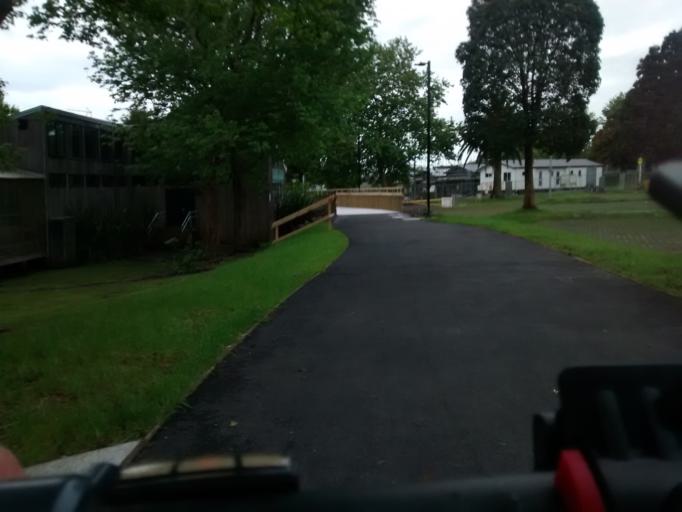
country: NZ
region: Auckland
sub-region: Auckland
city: Rosebank
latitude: -36.8825
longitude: 174.7048
